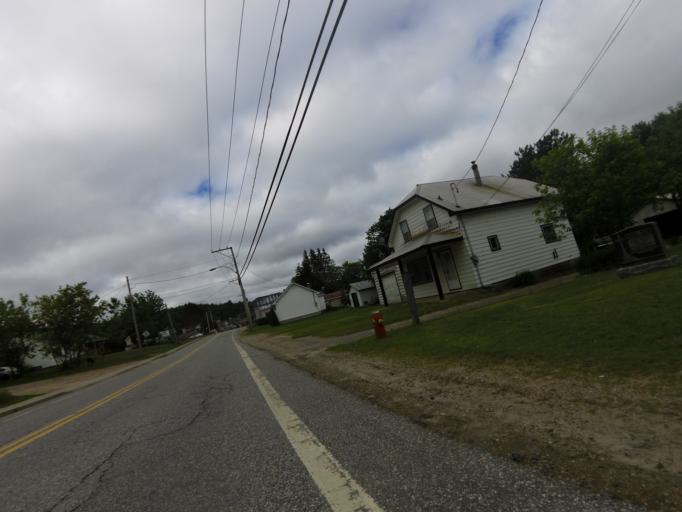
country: CA
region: Quebec
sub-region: Outaouais
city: Shawville
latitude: 45.8476
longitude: -76.4310
